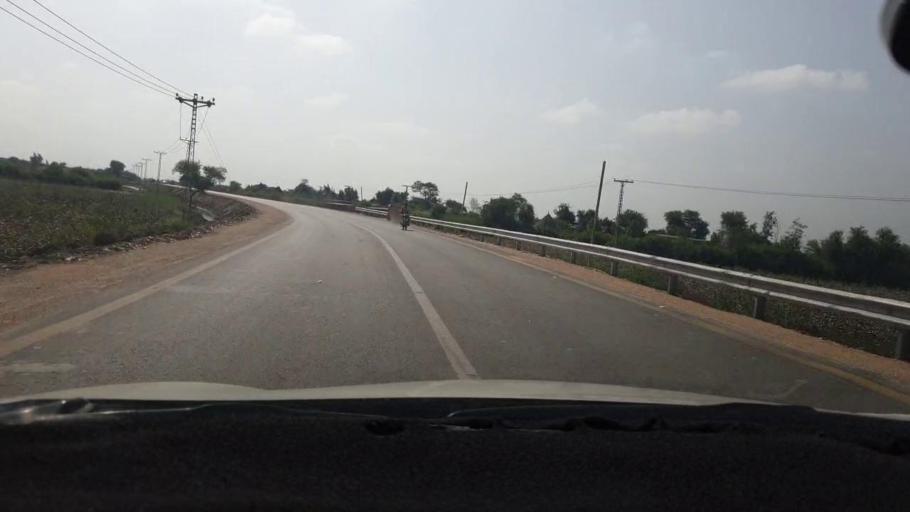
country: PK
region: Sindh
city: Mirpur Khas
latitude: 25.7666
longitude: 69.0716
